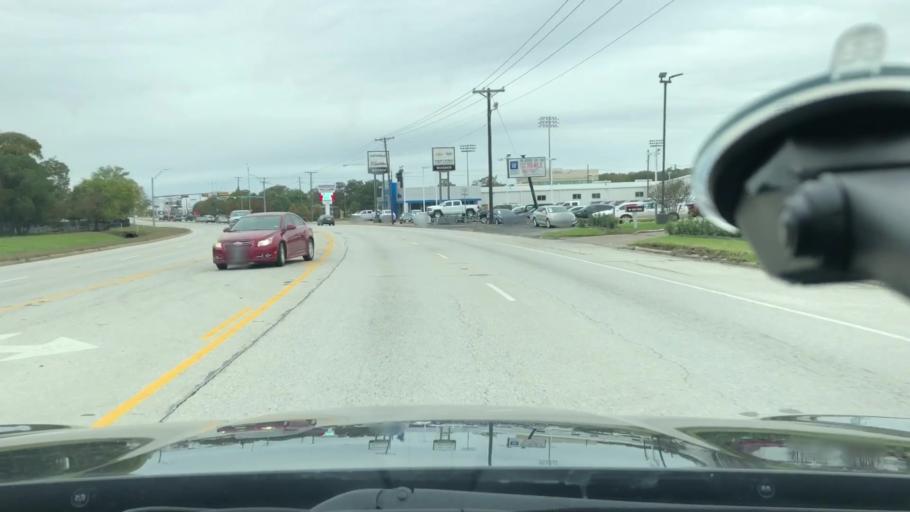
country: US
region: Texas
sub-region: Kaufman County
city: Terrell
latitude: 32.7390
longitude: -96.2917
